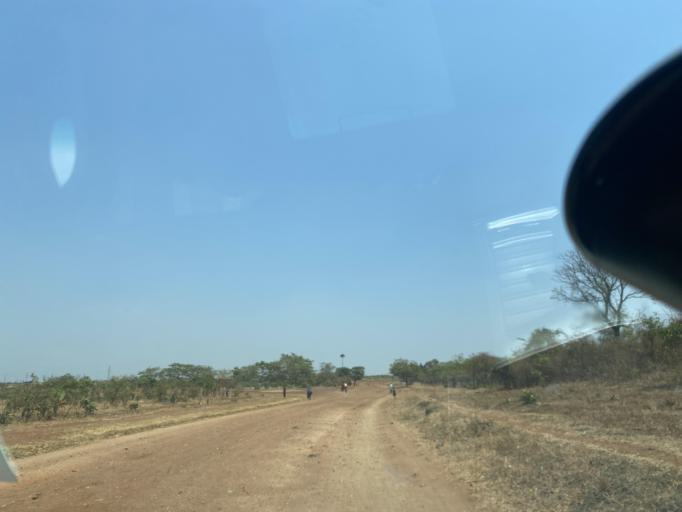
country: ZM
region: Lusaka
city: Kafue
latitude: -15.5187
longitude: 27.9412
